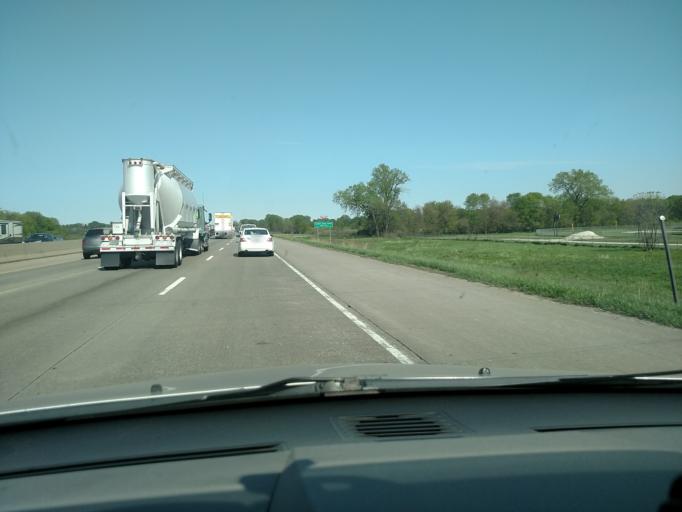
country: US
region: Iowa
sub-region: Polk County
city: Saylorville
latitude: 41.6495
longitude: -93.6417
